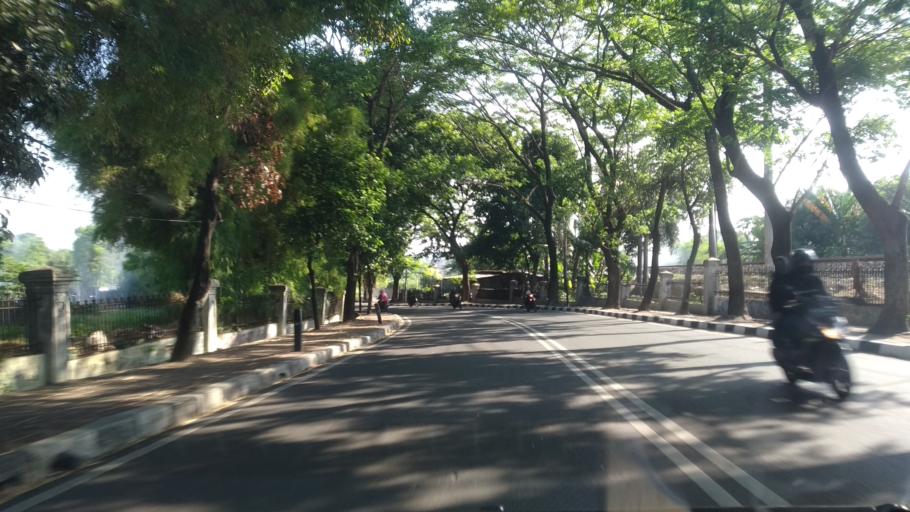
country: ID
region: Banten
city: South Tangerang
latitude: -6.2533
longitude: 106.7696
